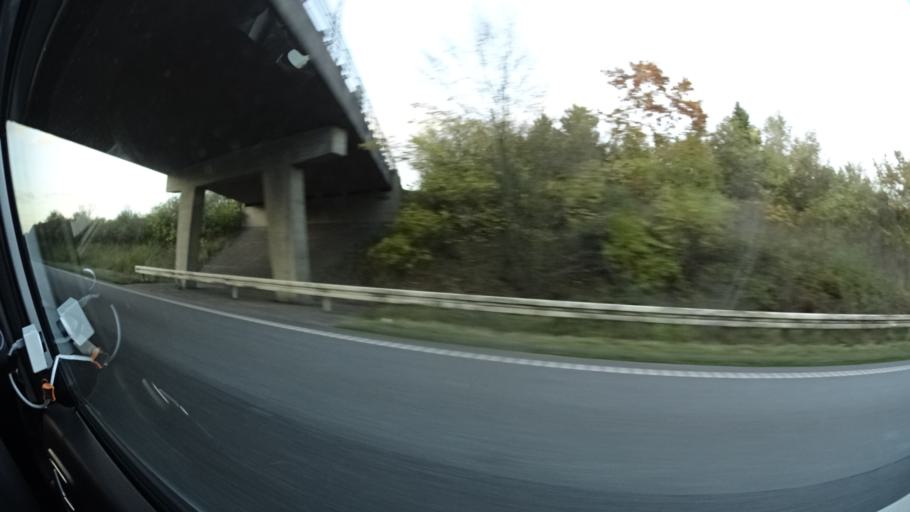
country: DK
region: South Denmark
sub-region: Assens Kommune
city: Tommerup Stationsby
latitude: 55.3923
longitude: 10.1962
